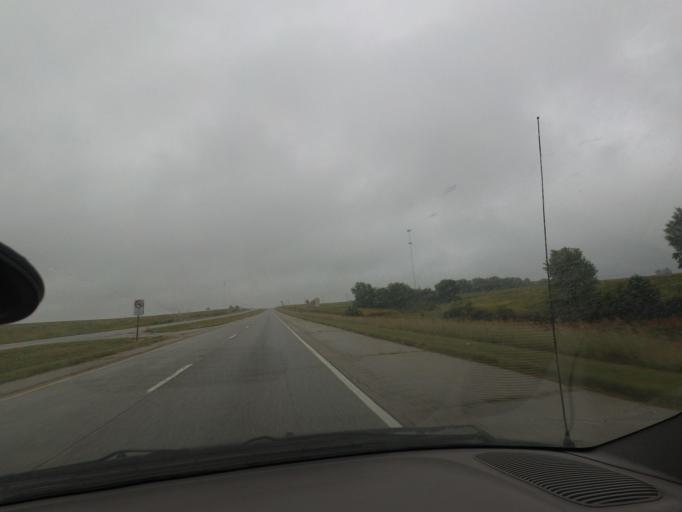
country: US
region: Illinois
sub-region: Pike County
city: Barry
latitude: 39.7011
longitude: -91.0273
